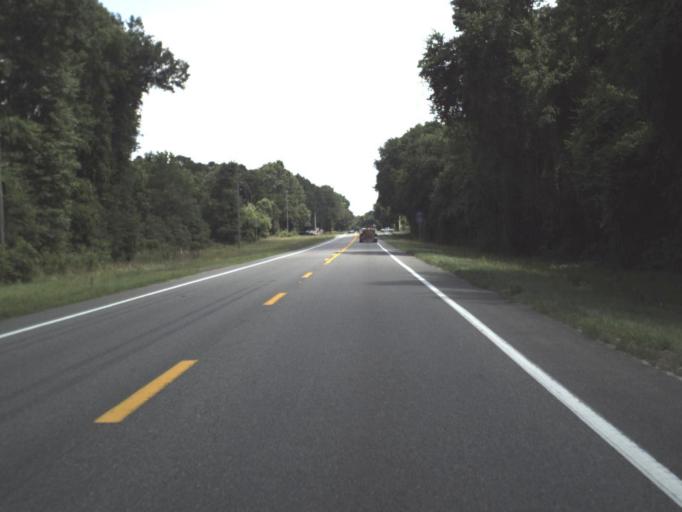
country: US
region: Florida
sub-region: Alachua County
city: High Springs
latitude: 29.8564
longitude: -82.6431
